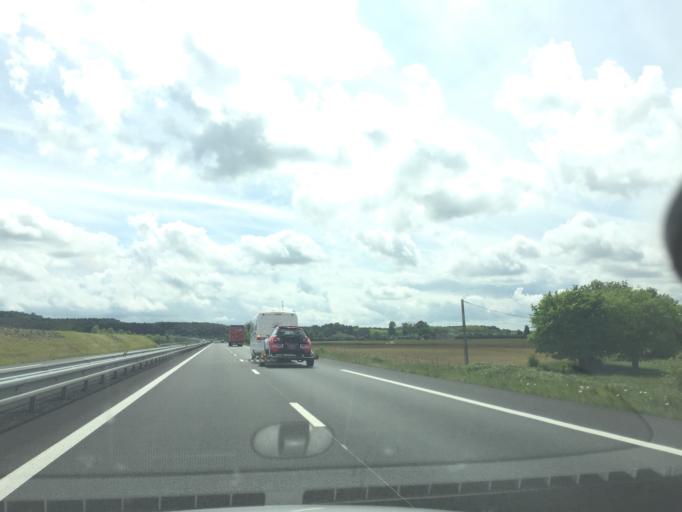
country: FR
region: Pays de la Loire
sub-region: Departement de la Sarthe
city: Teloche
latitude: 47.8671
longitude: 0.3014
